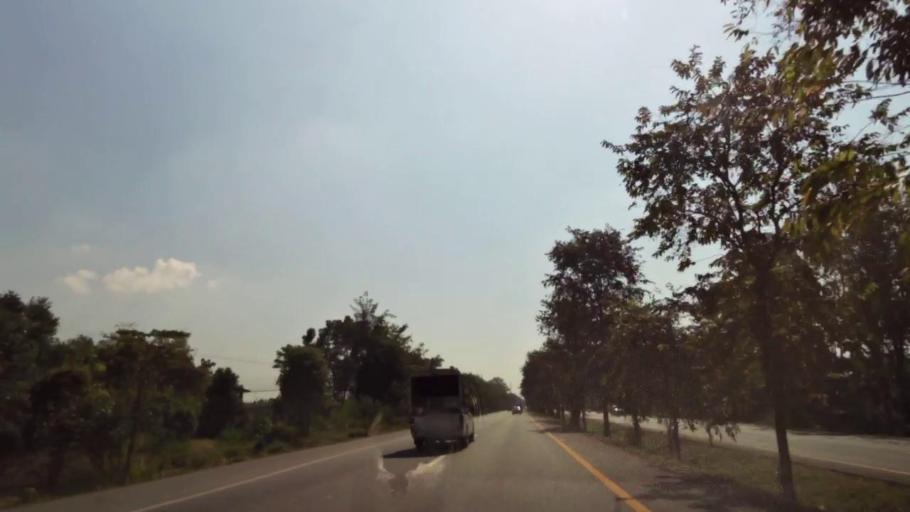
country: TH
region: Phichit
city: Bueng Na Rang
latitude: 16.1068
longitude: 100.1258
